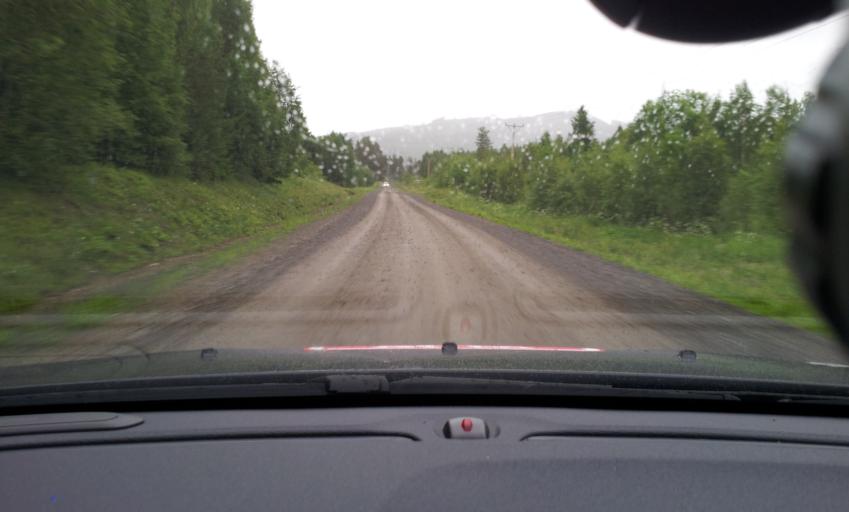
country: SE
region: Jaemtland
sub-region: Ragunda Kommun
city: Hammarstrand
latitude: 63.1374
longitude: 16.2412
